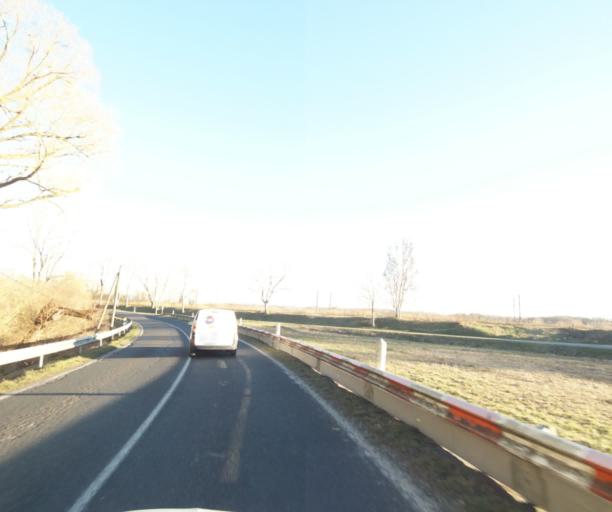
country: FR
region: Lorraine
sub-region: Departement de Meurthe-et-Moselle
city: Art-sur-Meurthe
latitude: 48.6467
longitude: 6.2792
